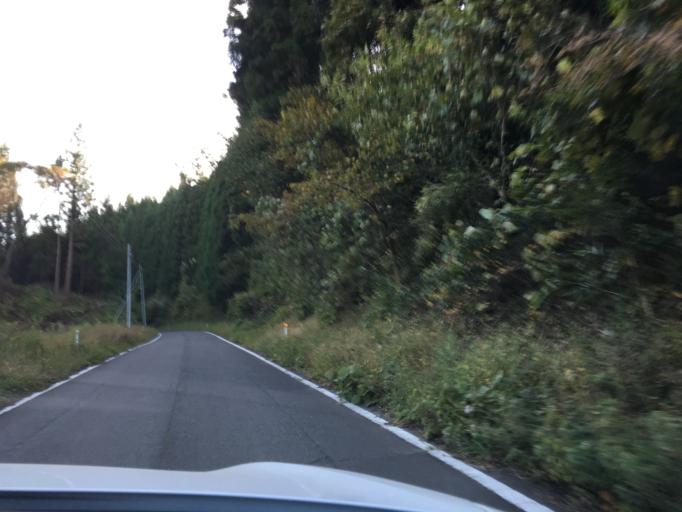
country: JP
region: Fukushima
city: Ishikawa
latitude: 37.2518
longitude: 140.6075
